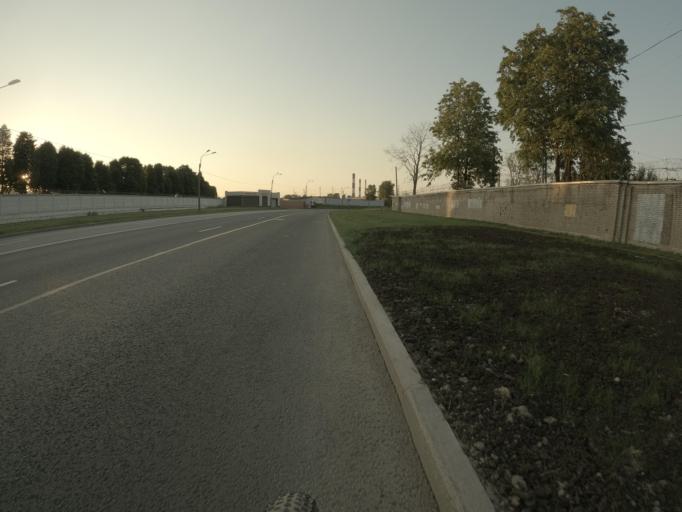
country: RU
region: St.-Petersburg
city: Avtovo
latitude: 59.8584
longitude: 30.2835
